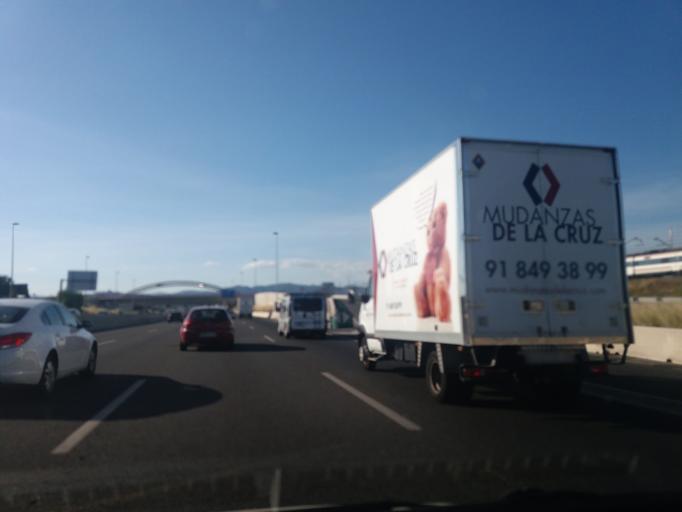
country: ES
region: Madrid
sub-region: Provincia de Madrid
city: Las Matas
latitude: 40.5442
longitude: -3.8938
